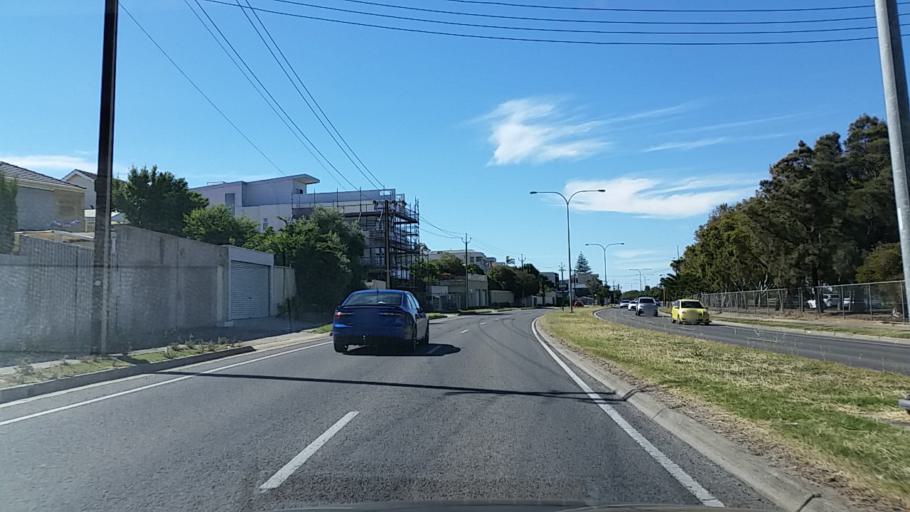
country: AU
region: South Australia
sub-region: Charles Sturt
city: Grange
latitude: -34.8966
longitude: 138.4893
